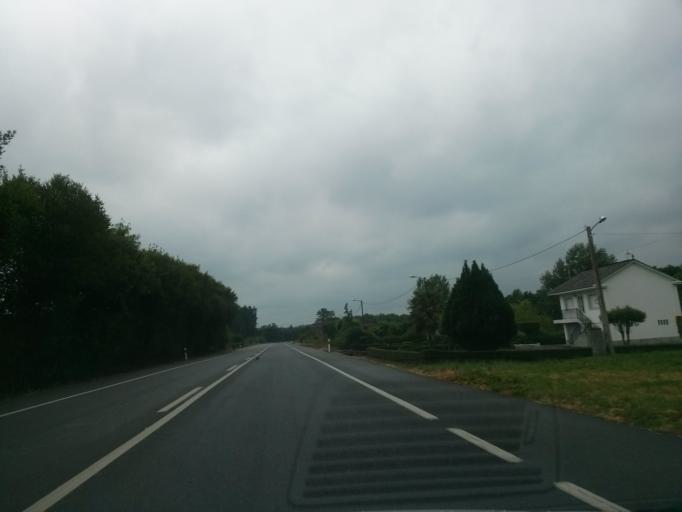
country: ES
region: Galicia
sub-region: Provincia de Lugo
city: Begonte
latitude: 43.1640
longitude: -7.7067
